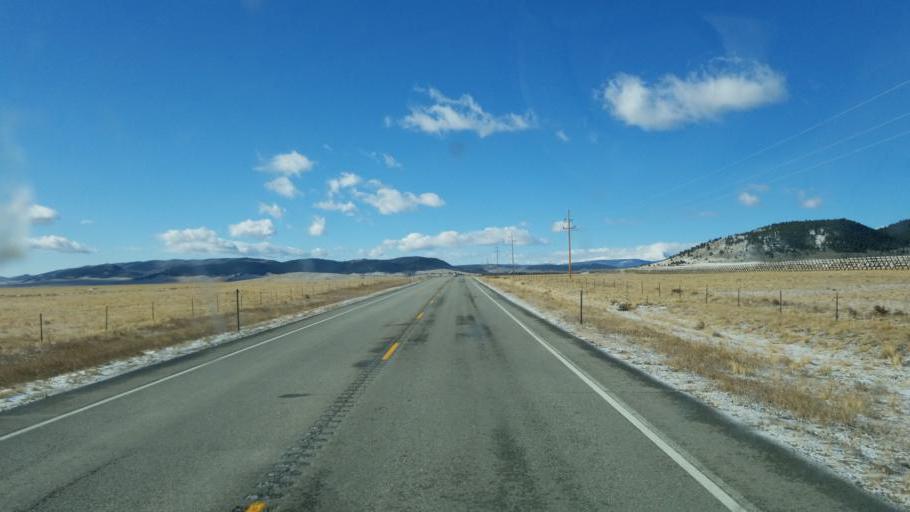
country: US
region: Colorado
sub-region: Park County
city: Fairplay
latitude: 39.3237
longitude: -105.8751
